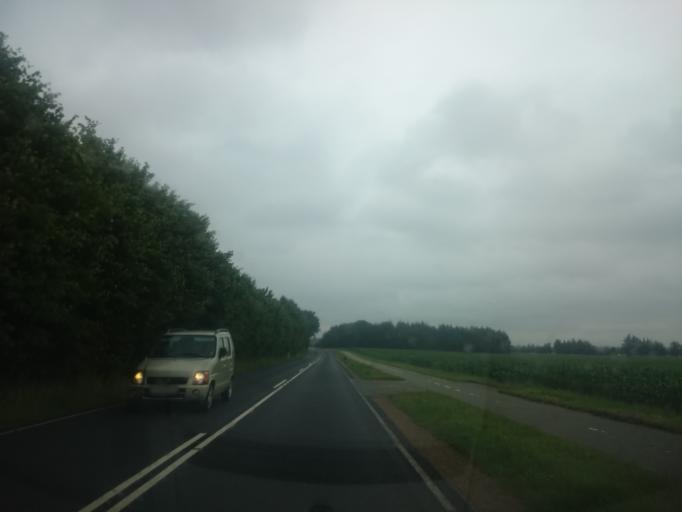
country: DK
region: South Denmark
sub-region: Vejen Kommune
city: Holsted
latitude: 55.6143
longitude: 8.8023
